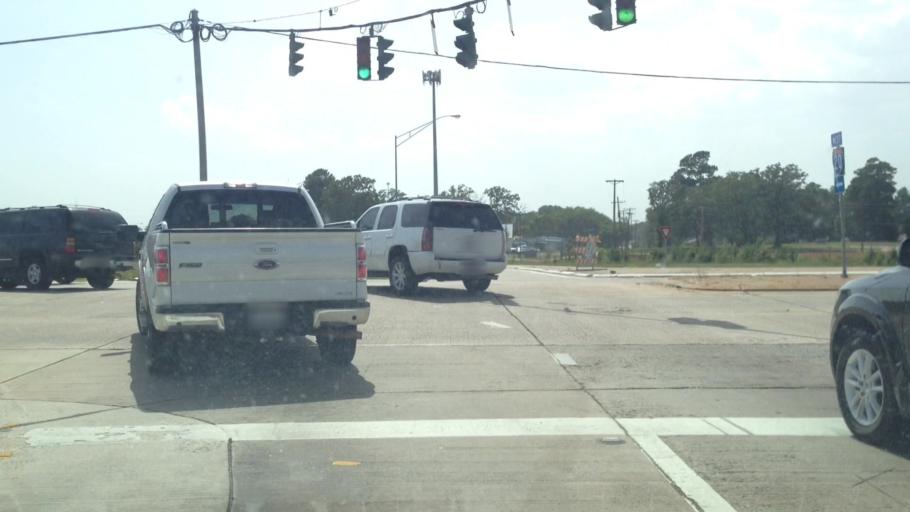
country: US
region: Louisiana
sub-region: Caddo Parish
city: Greenwood
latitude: 32.4514
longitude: -93.8654
